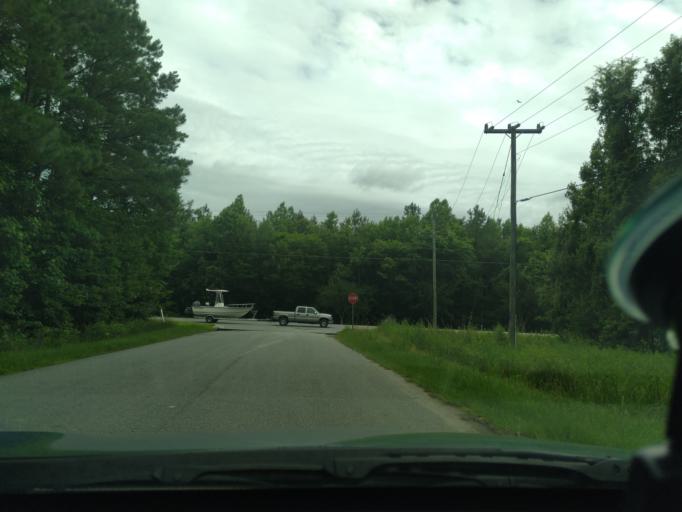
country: US
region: North Carolina
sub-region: Washington County
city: Plymouth
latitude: 35.8696
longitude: -76.7115
